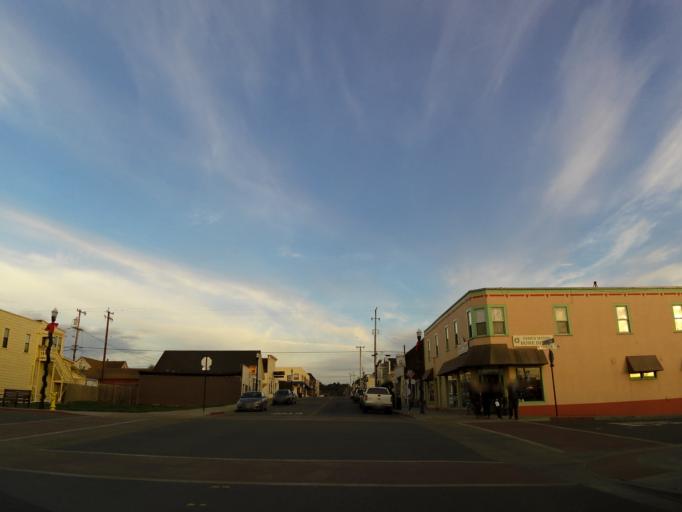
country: US
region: California
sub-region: Mendocino County
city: Fort Bragg
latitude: 39.4442
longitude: -123.8048
